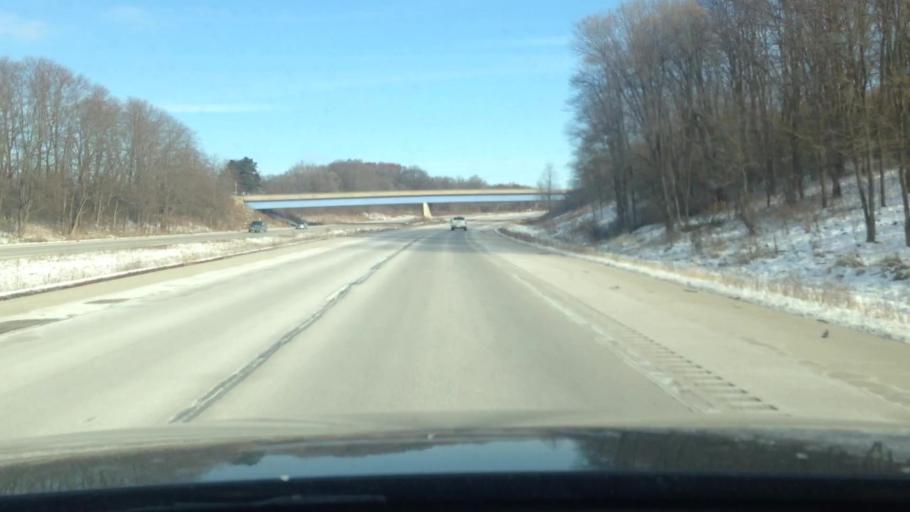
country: US
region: Wisconsin
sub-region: Walworth County
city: Potter Lake
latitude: 42.8248
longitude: -88.3560
